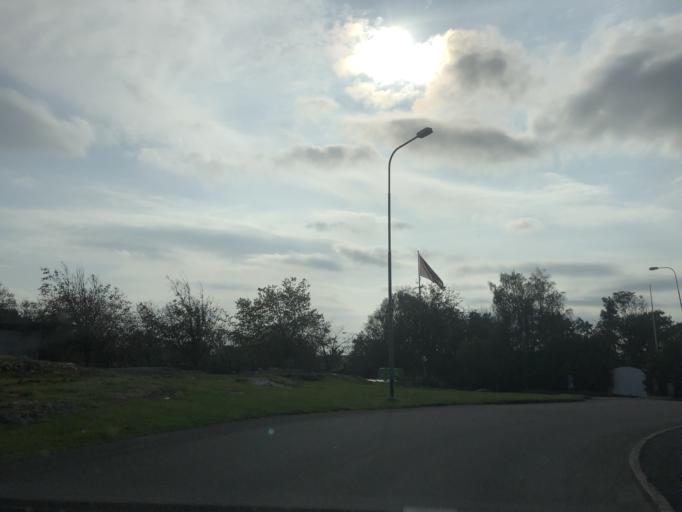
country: SE
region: Vaestra Goetaland
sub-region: Goteborg
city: Majorna
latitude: 57.6515
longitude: 11.8967
